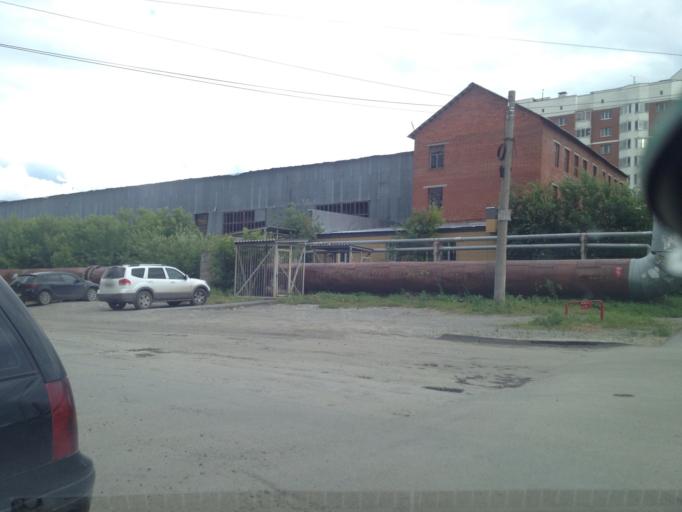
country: RU
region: Sverdlovsk
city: Yekaterinburg
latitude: 56.8743
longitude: 60.5418
